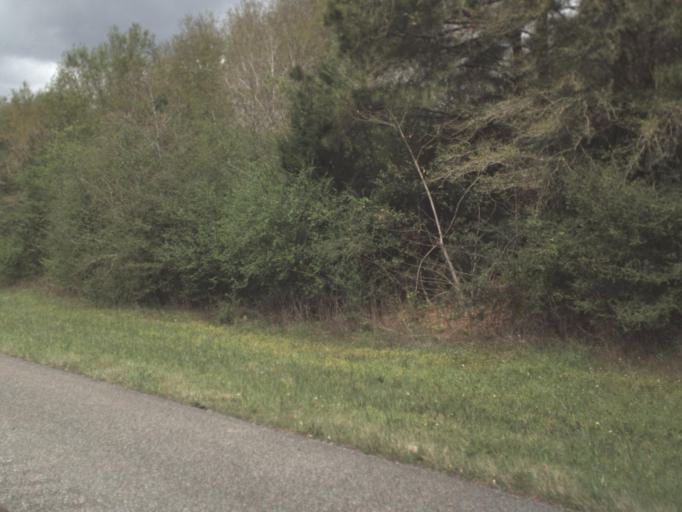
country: US
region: Florida
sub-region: Okaloosa County
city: Crestview
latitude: 30.6956
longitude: -86.7599
